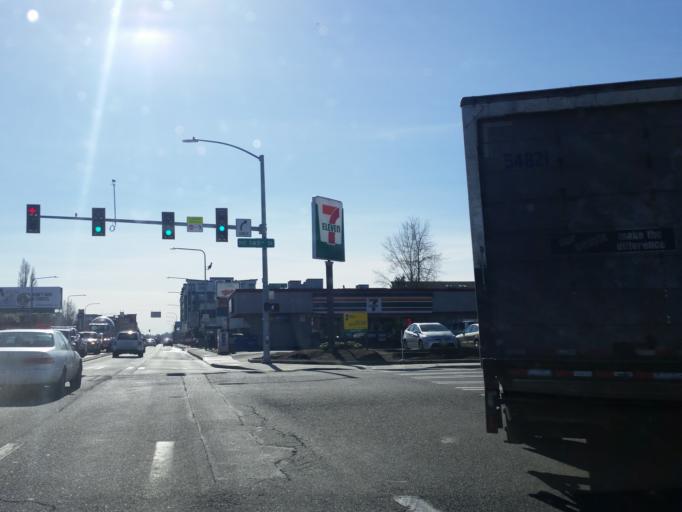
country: US
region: Washington
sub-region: King County
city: Lake Forest Park
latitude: 47.7341
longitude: -122.2926
